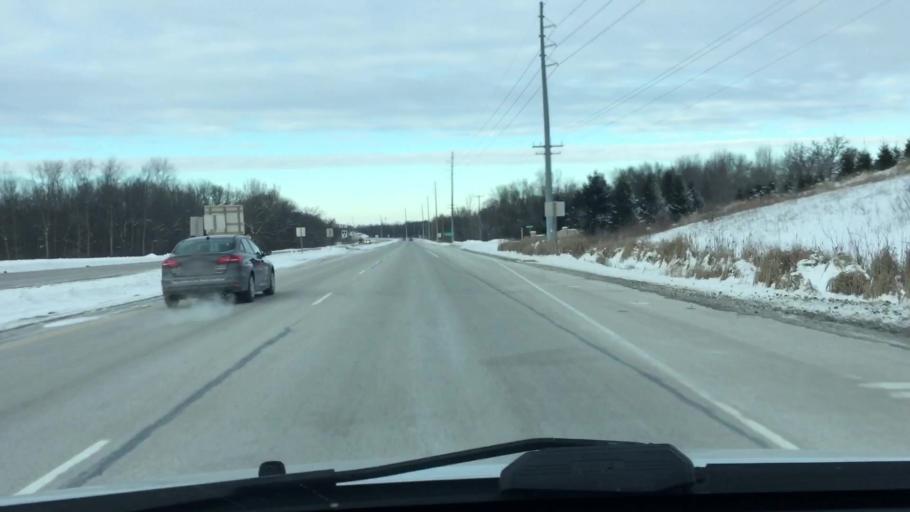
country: US
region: Wisconsin
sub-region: Waukesha County
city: Sussex
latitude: 43.0851
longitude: -88.2058
